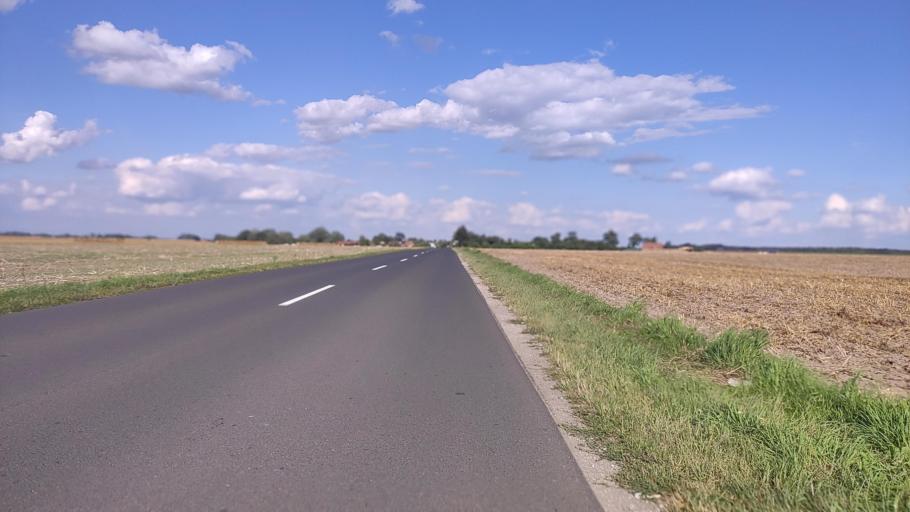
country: PL
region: Greater Poland Voivodeship
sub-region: Powiat poznanski
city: Swarzedz
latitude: 52.4211
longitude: 17.1460
